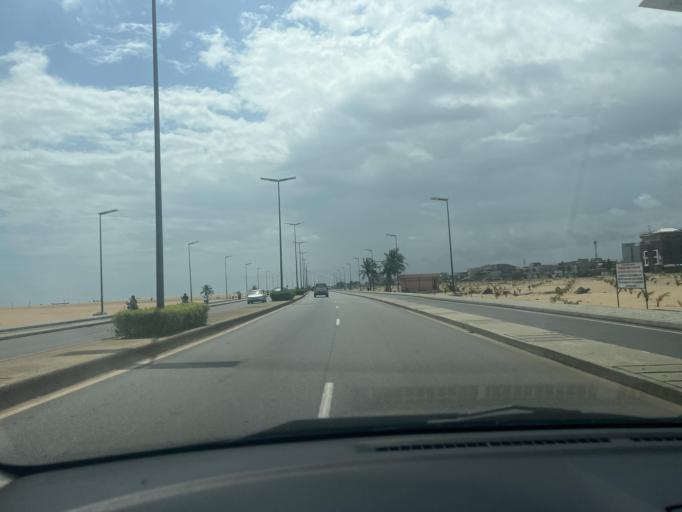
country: BJ
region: Littoral
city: Cotonou
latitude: 6.3489
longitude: 2.3712
